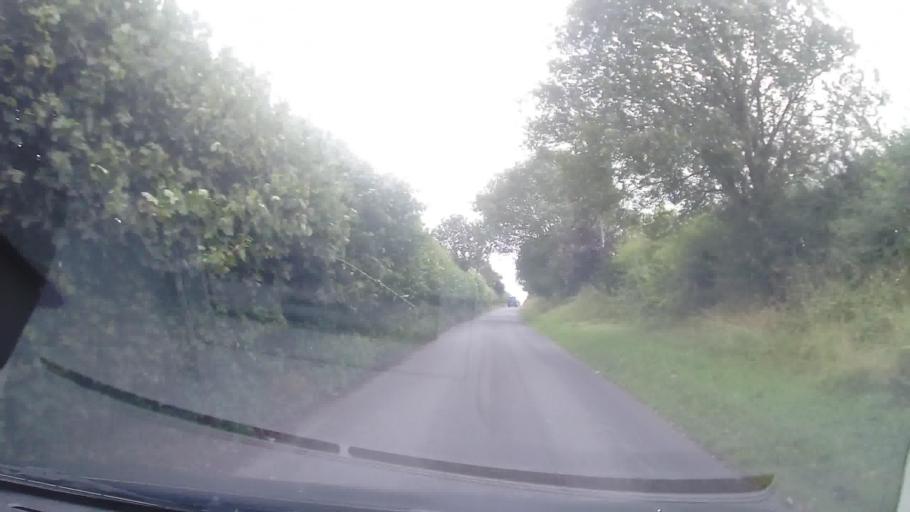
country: GB
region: Wales
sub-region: Sir Powys
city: Knighton
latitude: 52.3387
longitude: -3.0315
